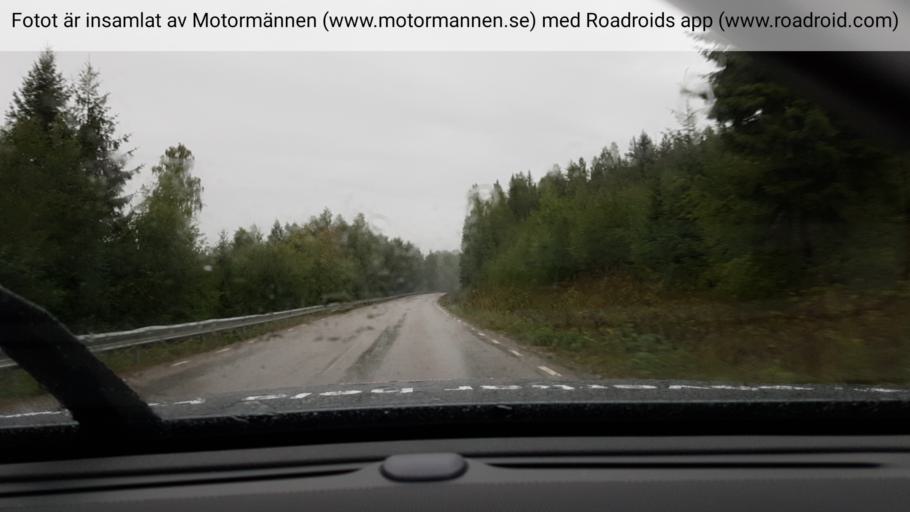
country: SE
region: Dalarna
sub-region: Faluns Kommun
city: Bjursas
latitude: 60.7472
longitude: 15.4142
